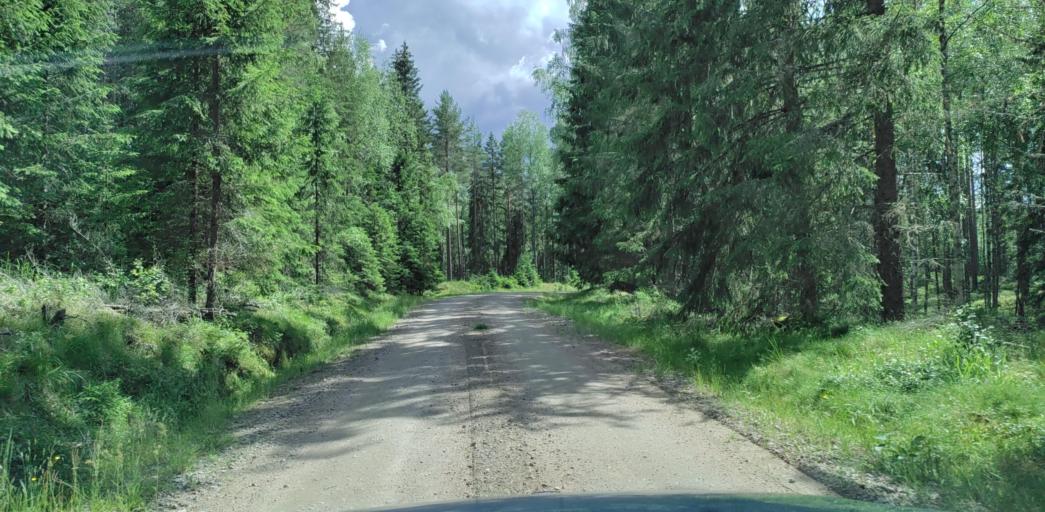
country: SE
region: Vaermland
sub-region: Hagfors Kommun
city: Ekshaerad
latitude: 60.0592
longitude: 13.3105
